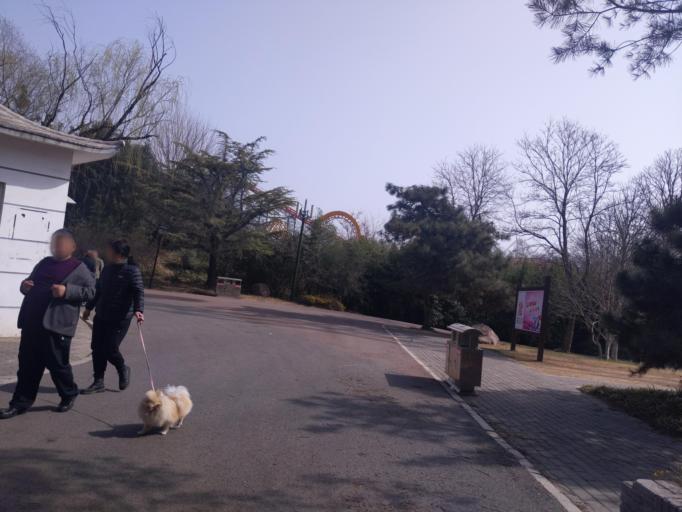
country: CN
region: Henan Sheng
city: Puyang
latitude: 35.7759
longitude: 114.9592
